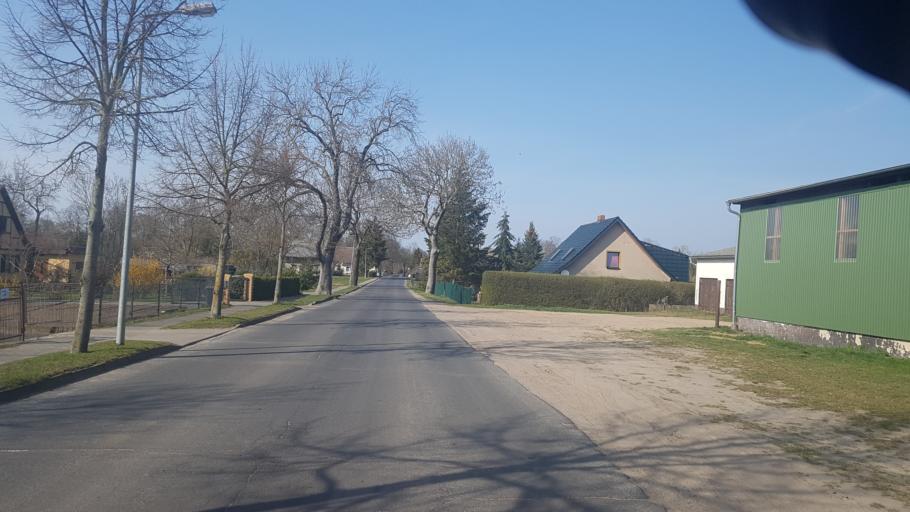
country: DE
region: Brandenburg
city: Prenzlau
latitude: 53.2258
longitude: 13.8430
